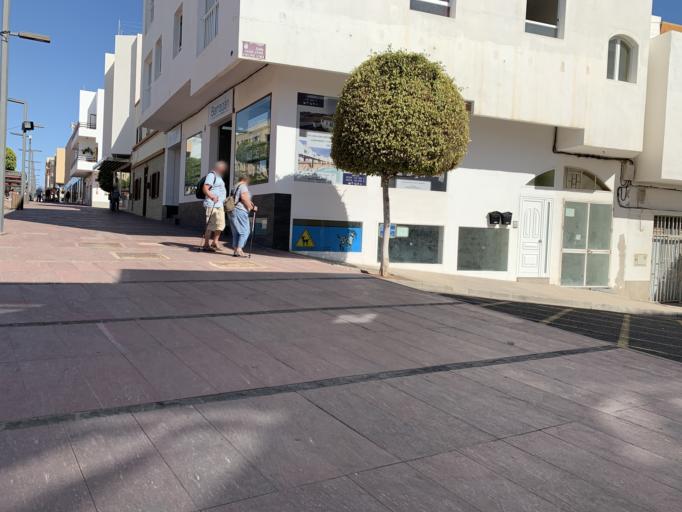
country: ES
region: Canary Islands
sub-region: Provincia de Las Palmas
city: Puerto del Rosario
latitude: 28.4962
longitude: -13.8613
